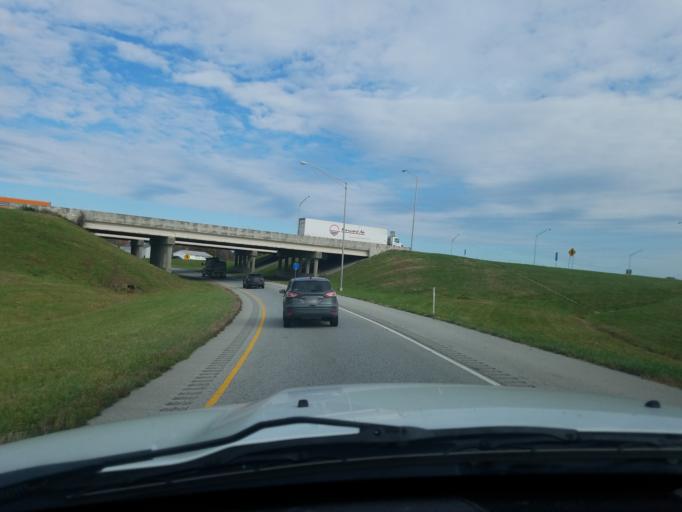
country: US
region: Indiana
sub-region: Clark County
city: Clarksville
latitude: 38.3450
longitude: -85.7518
